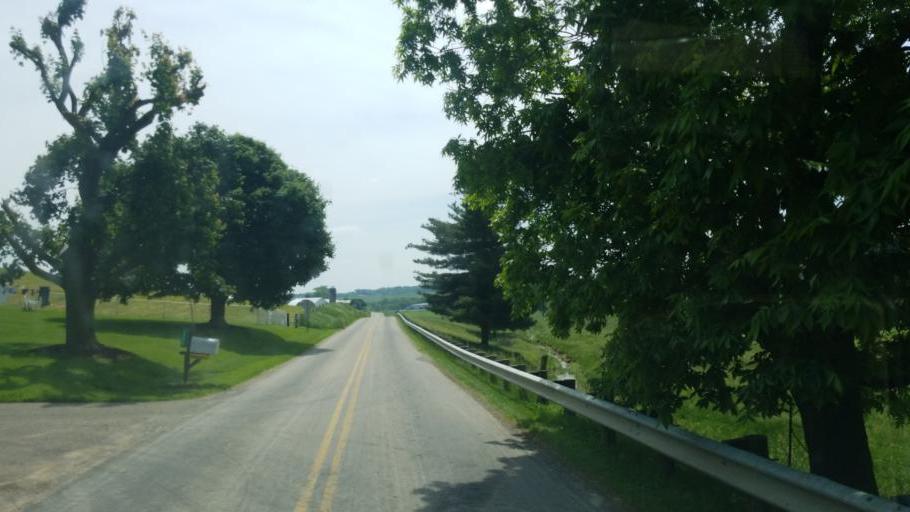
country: US
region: Ohio
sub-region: Tuscarawas County
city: Sugarcreek
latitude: 40.5096
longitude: -81.6853
